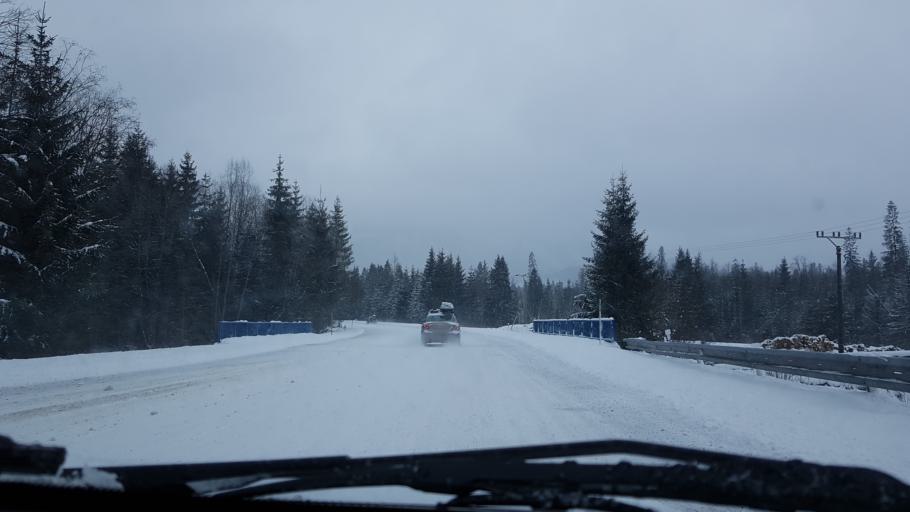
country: PL
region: Lesser Poland Voivodeship
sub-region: Powiat tatrzanski
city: Bukowina Tatrzanska
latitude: 49.2968
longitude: 20.1646
